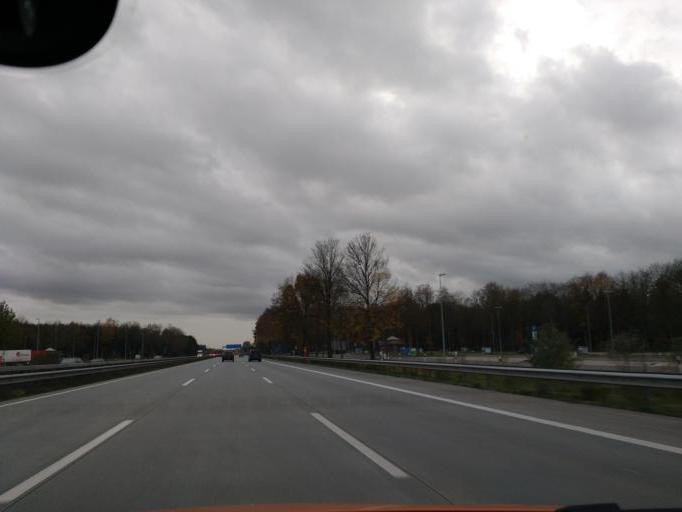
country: DE
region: Lower Saxony
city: Gyhum
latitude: 53.2023
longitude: 9.2982
